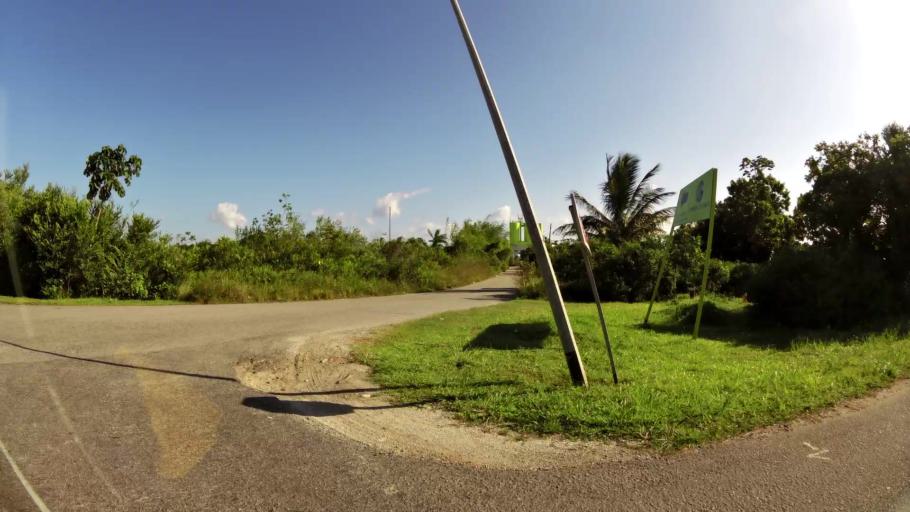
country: GF
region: Guyane
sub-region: Guyane
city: Matoury
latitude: 4.8604
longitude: -52.2753
